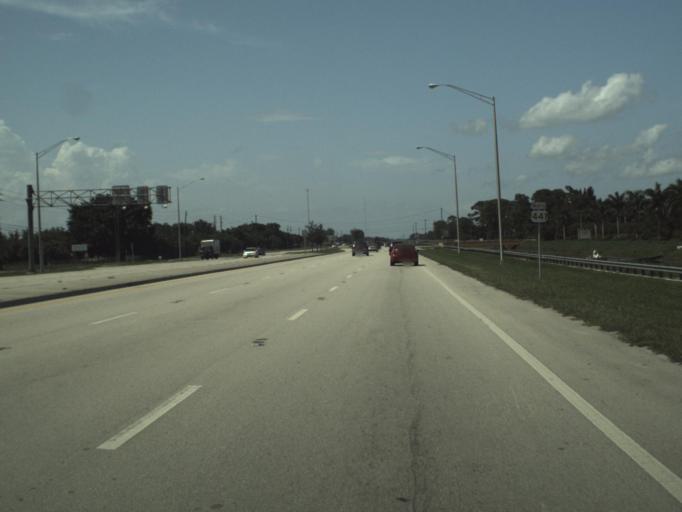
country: US
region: Florida
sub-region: Palm Beach County
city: Villages of Oriole
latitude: 26.5283
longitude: -80.2053
